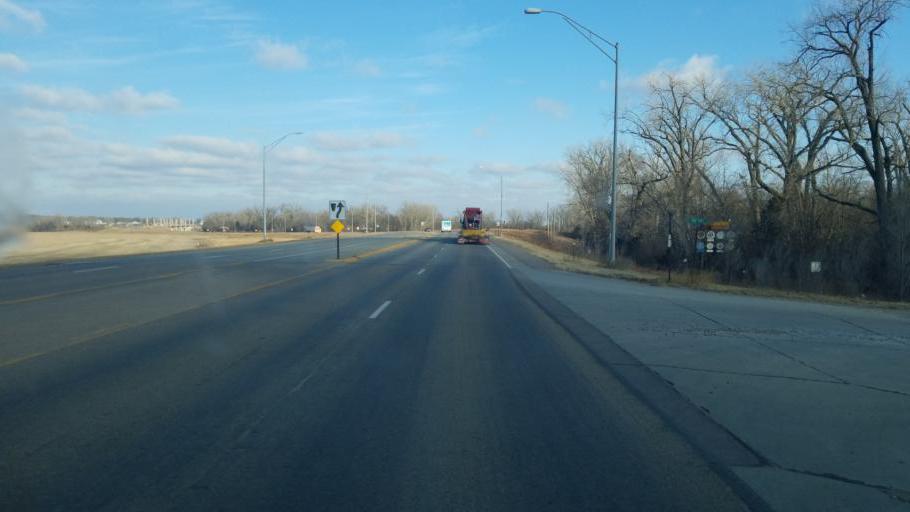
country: US
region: South Dakota
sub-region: Yankton County
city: Yankton
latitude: 42.8517
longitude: -97.3971
